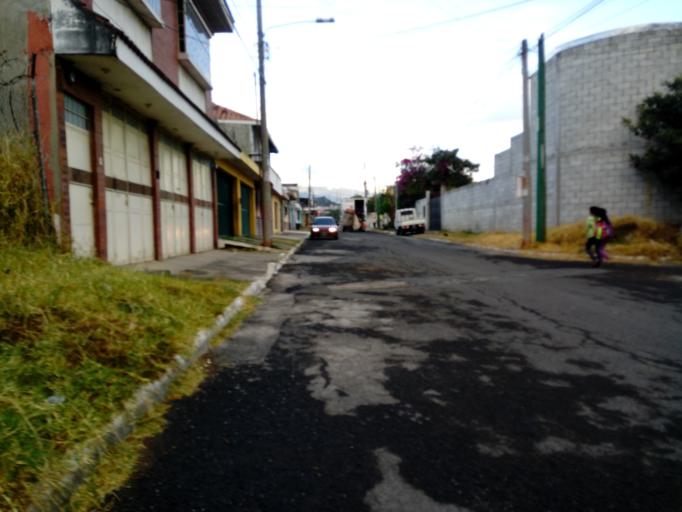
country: GT
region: Guatemala
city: Villa Nueva
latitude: 14.5330
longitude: -90.5820
